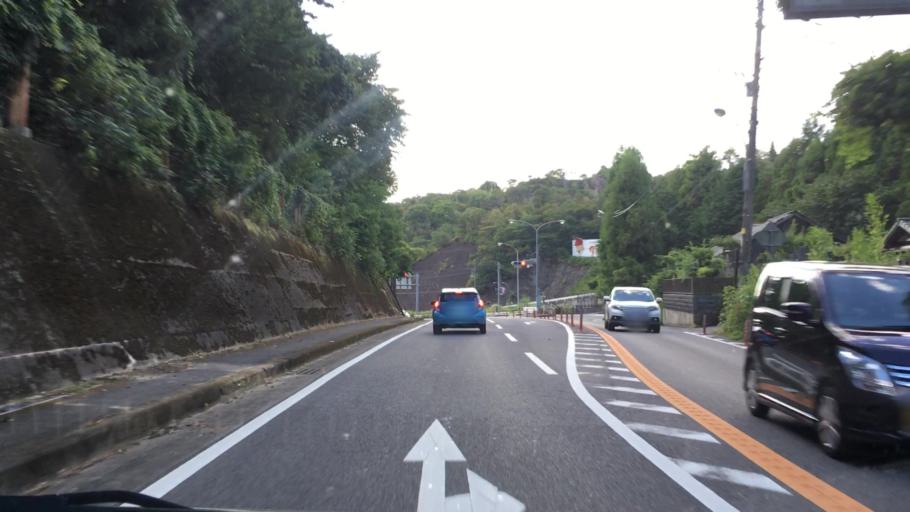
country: JP
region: Saga Prefecture
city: Imaricho-ko
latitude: 33.1917
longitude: 129.9125
